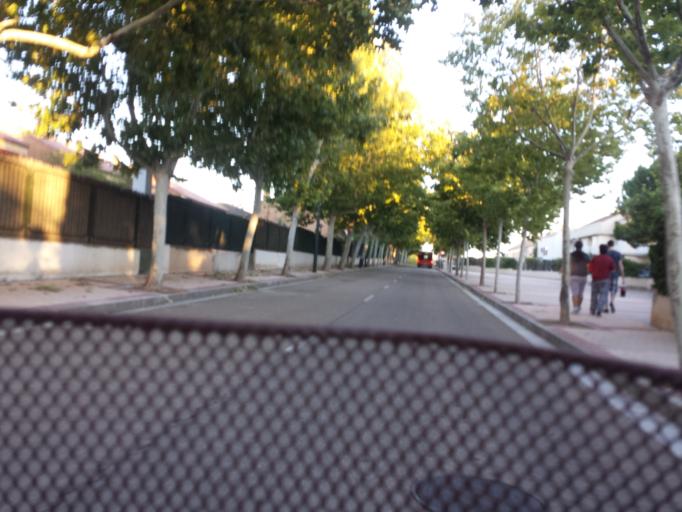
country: ES
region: Aragon
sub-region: Provincia de Zaragoza
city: Montecanal
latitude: 41.6288
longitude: -0.9444
